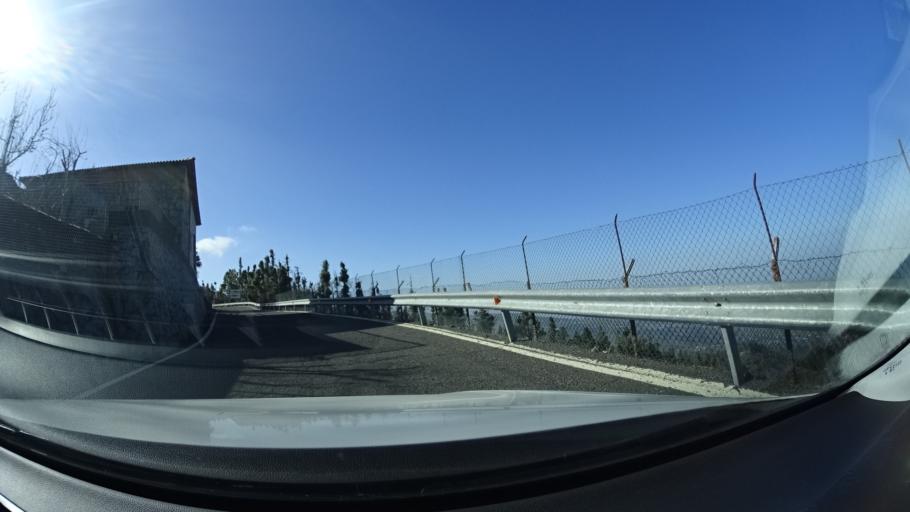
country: ES
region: Canary Islands
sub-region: Provincia de Las Palmas
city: San Bartolome
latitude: 27.9686
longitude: -15.5636
